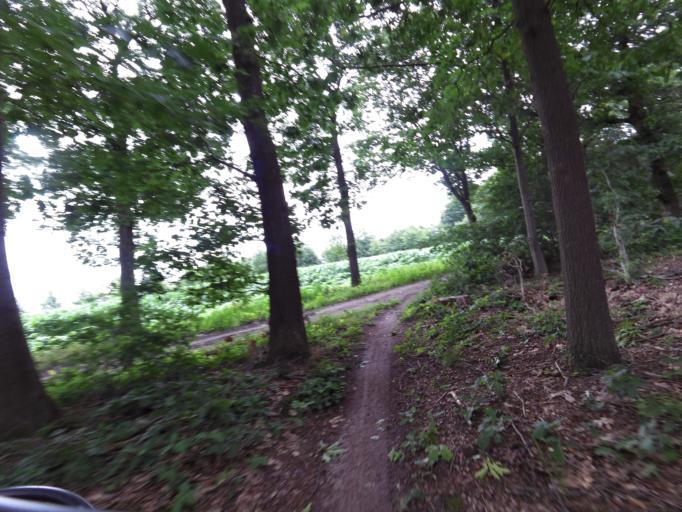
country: NL
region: North Brabant
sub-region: Gemeente Veghel
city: Keldonk
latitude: 51.5439
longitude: 5.5594
